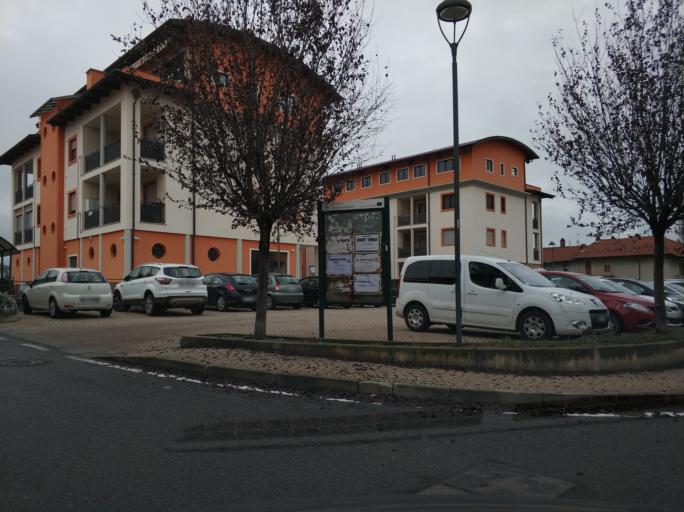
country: IT
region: Piedmont
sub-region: Provincia di Torino
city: Villanova Canavese
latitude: 45.2431
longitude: 7.5536
